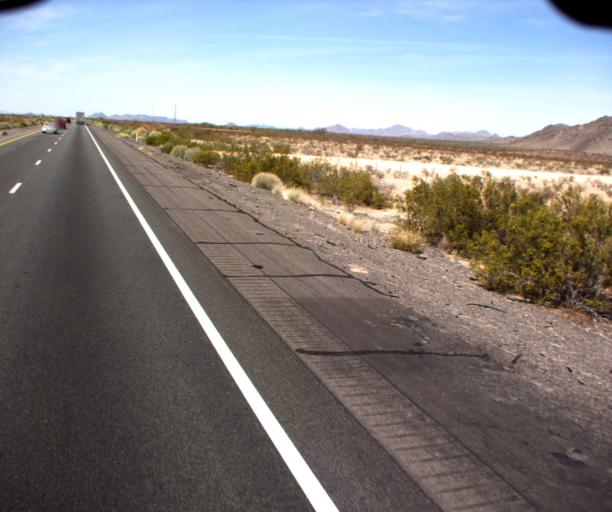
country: US
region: Arizona
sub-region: La Paz County
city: Salome
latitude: 33.5833
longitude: -113.4460
